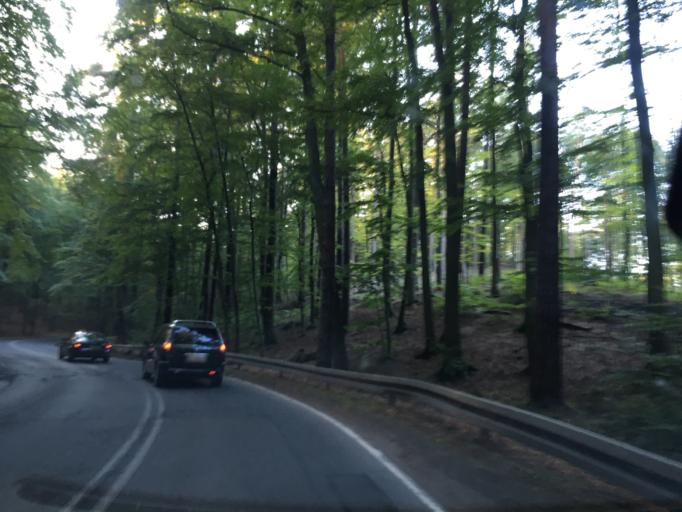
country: PL
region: Pomeranian Voivodeship
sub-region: Gdynia
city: Wielki Kack
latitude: 54.4582
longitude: 18.5119
